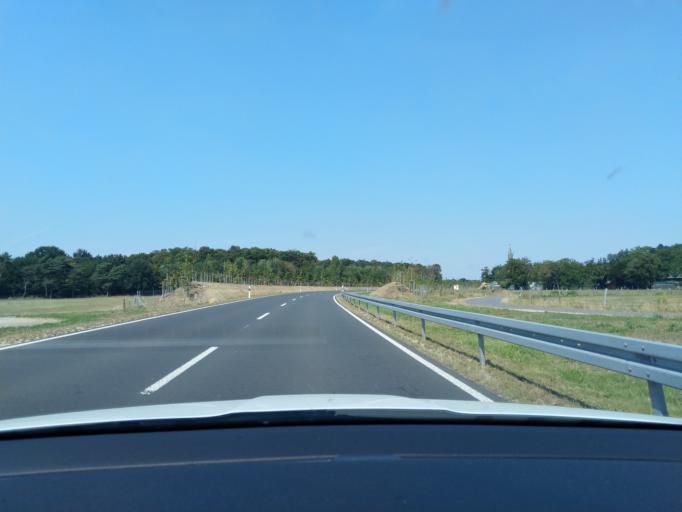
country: DE
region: North Rhine-Westphalia
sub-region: Regierungsbezirk Koln
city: Wassenberg
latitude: 51.1065
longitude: 6.2061
